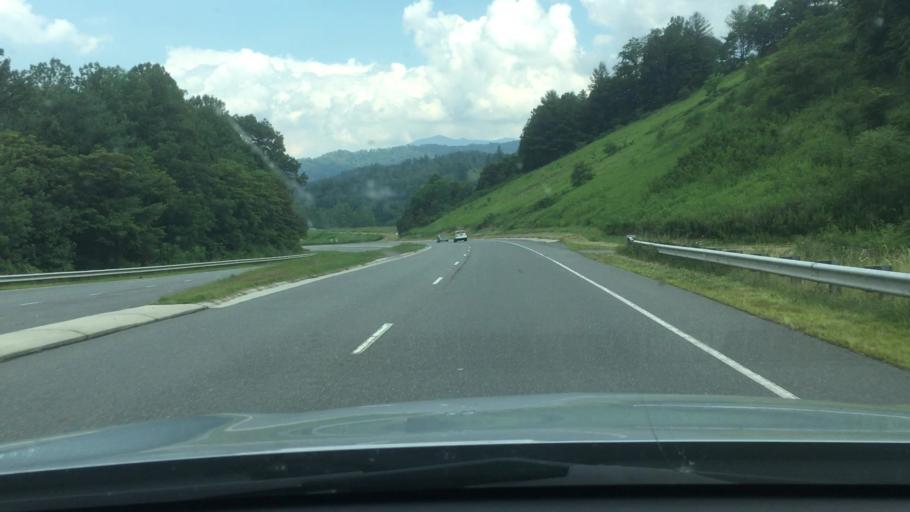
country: US
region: North Carolina
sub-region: Yancey County
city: Burnsville
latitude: 35.9118
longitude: -82.3902
